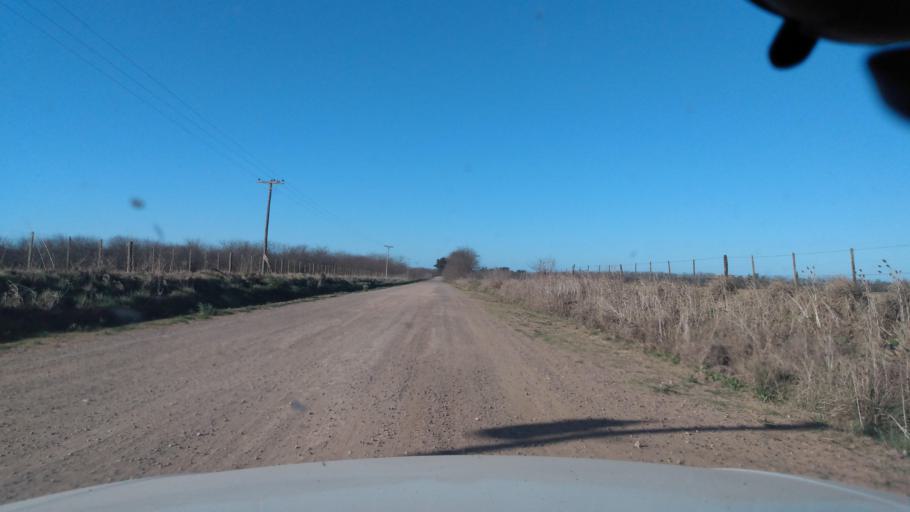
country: AR
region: Buenos Aires
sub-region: Partido de Mercedes
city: Mercedes
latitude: -34.6160
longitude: -59.3335
